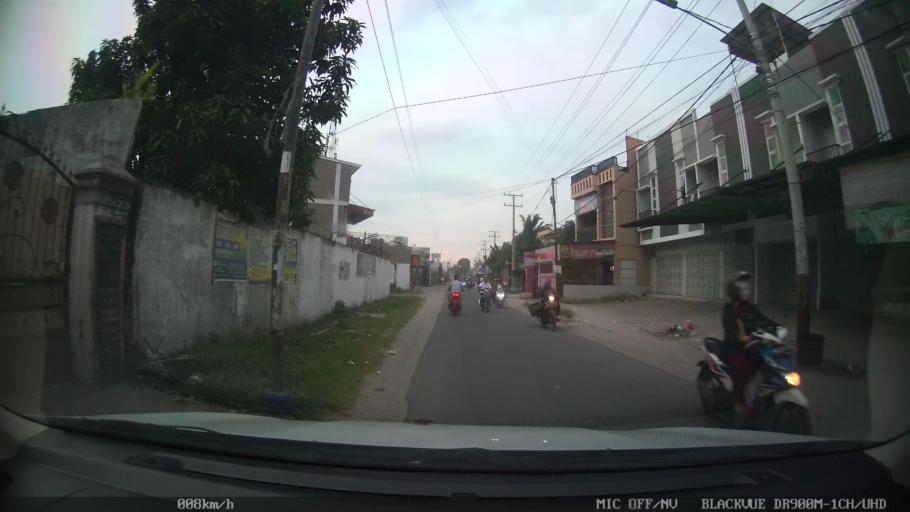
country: ID
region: North Sumatra
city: Sunggal
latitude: 3.5831
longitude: 98.5918
